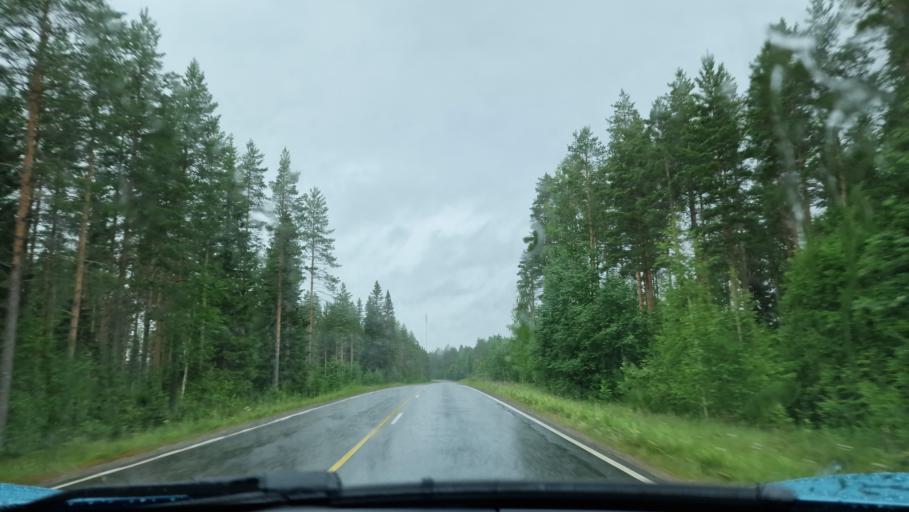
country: FI
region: Southern Ostrobothnia
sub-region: Jaerviseutu
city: Soini
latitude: 62.8140
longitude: 24.3578
